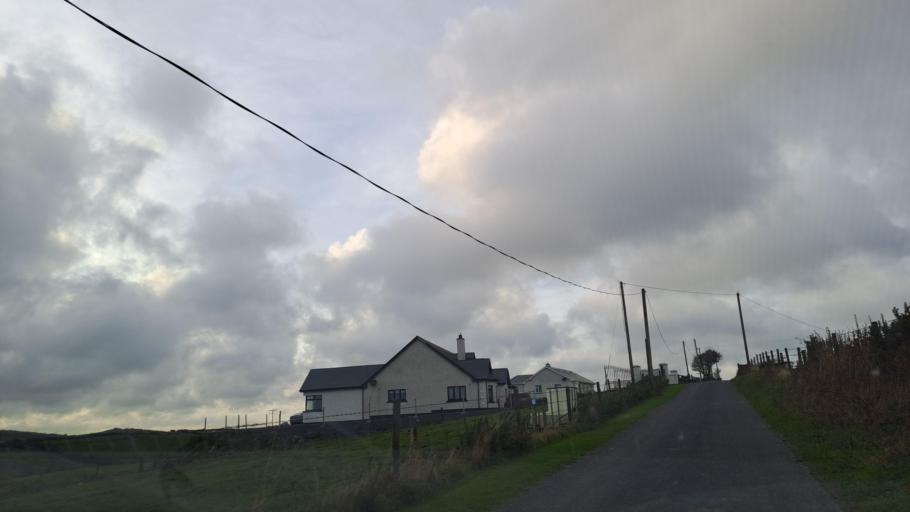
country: IE
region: Ulster
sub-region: County Monaghan
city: Carrickmacross
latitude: 54.0252
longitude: -6.7712
